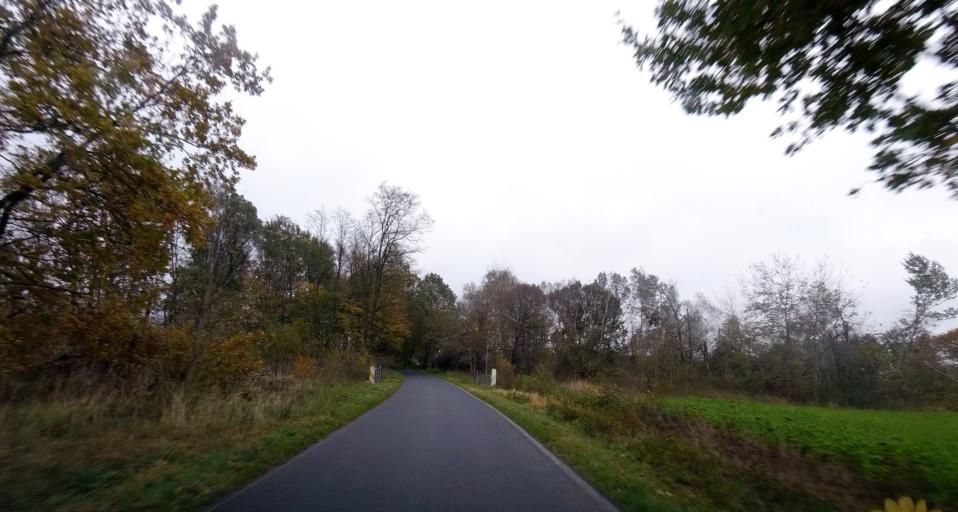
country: DE
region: Brandenburg
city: Niedergorsdorf
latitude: 52.0010
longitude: 12.9570
